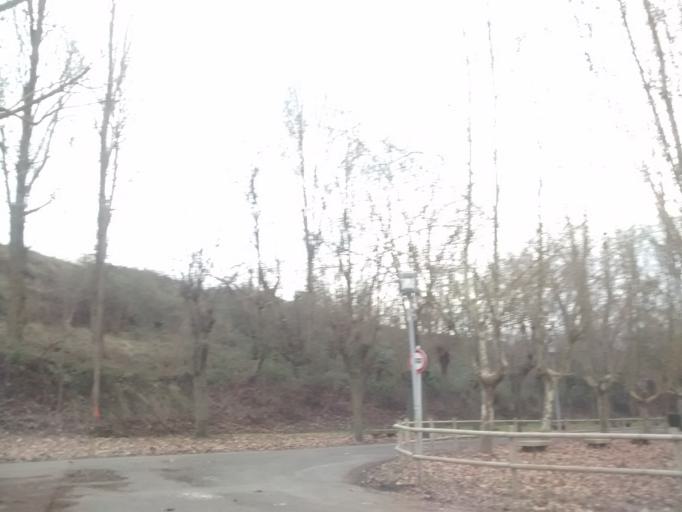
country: ES
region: La Rioja
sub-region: Provincia de La Rioja
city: Haro
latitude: 42.5733
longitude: -2.8641
